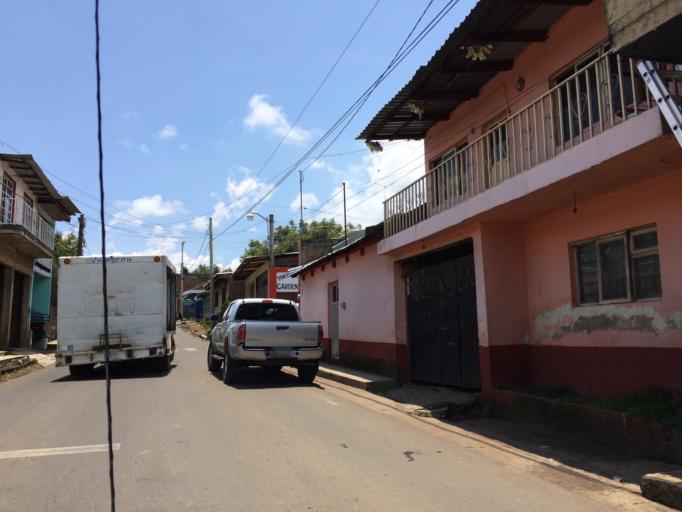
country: MX
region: Michoacan
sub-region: Periban
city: San Francisco Periban
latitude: 19.5561
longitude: -102.3985
